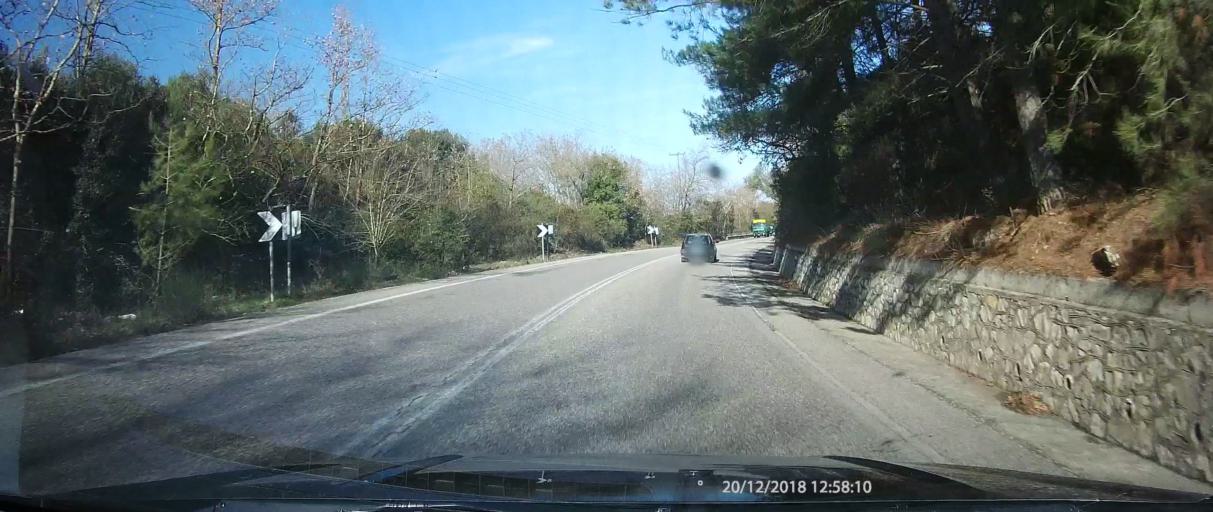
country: GR
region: West Greece
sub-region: Nomos Aitolias kai Akarnanias
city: Pappadhatai
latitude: 38.5339
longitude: 21.3753
